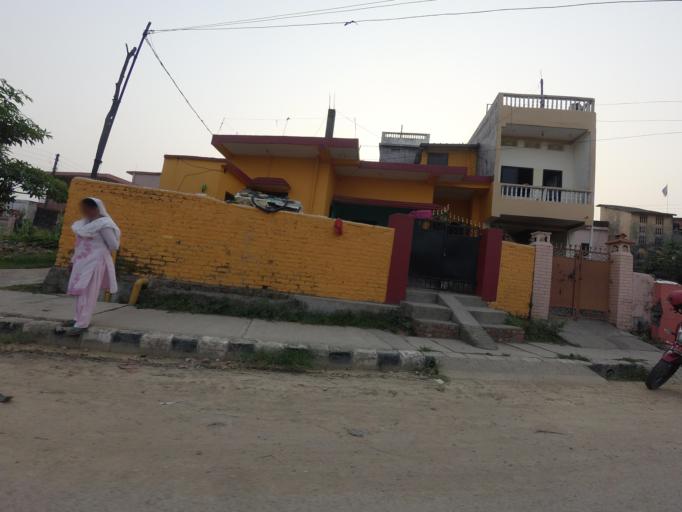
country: NP
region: Western Region
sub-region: Lumbini Zone
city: Bhairahawa
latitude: 27.5087
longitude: 83.4641
